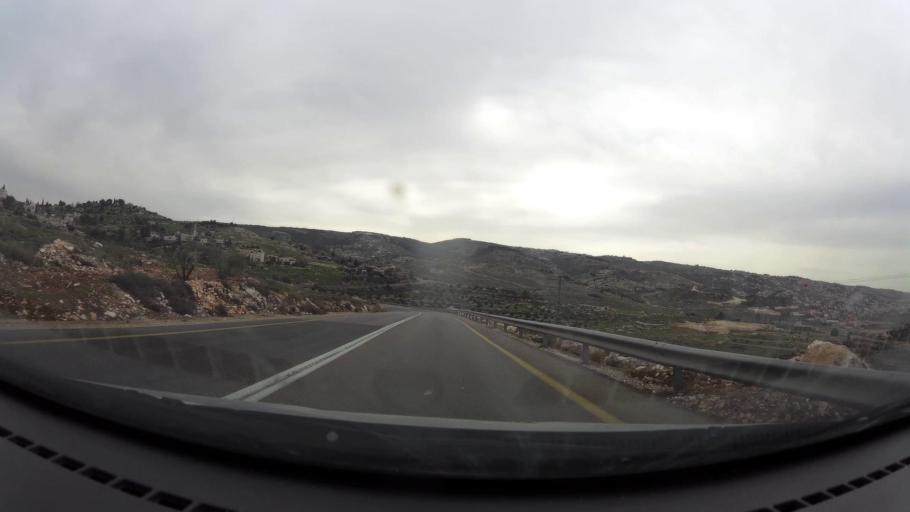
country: PS
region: West Bank
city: Surif
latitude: 31.6719
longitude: 35.0697
